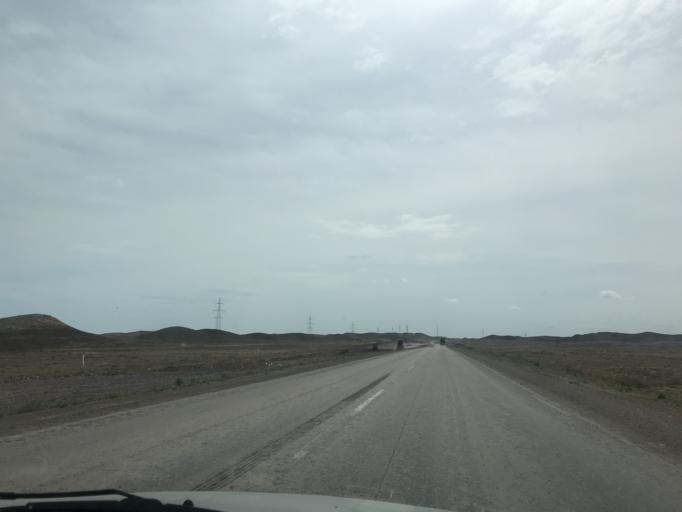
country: KZ
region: Zhambyl
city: Mynaral
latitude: 45.3640
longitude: 73.6674
